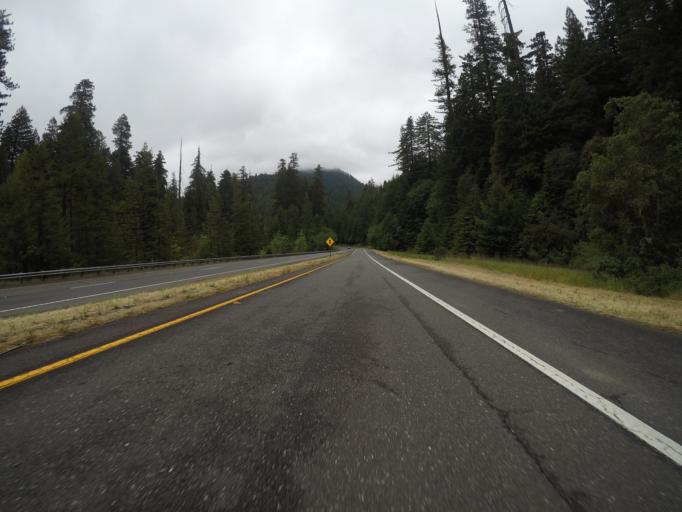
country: US
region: California
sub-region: Humboldt County
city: Rio Dell
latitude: 40.4453
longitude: -124.0398
